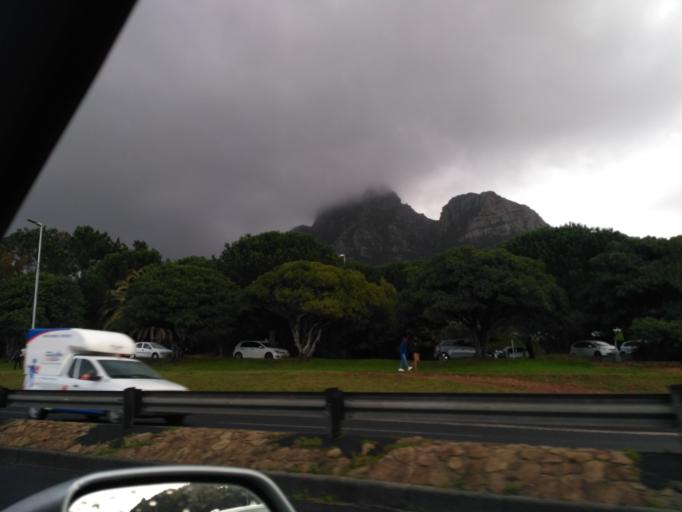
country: ZA
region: Western Cape
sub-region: City of Cape Town
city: Rosebank
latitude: -33.9546
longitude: 18.4645
